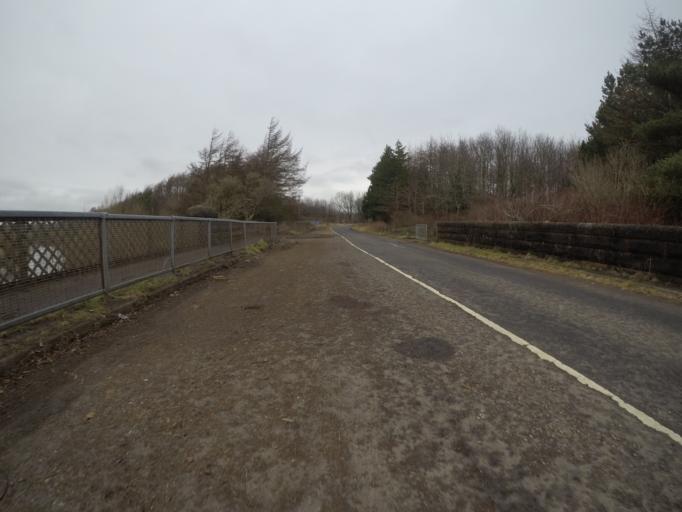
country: GB
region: Scotland
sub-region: North Ayrshire
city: Kilwinning
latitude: 55.6404
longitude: -4.6910
